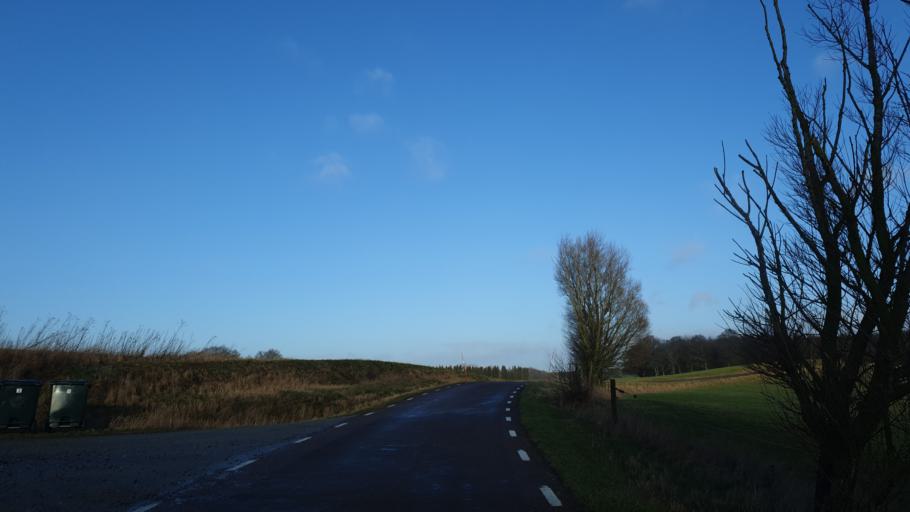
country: SE
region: Skane
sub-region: Svedala Kommun
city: Svedala
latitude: 55.4985
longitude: 13.2890
